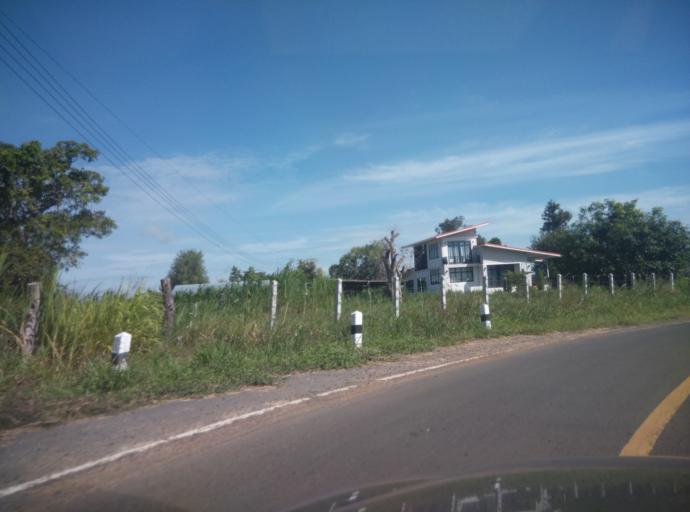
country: TH
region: Sisaket
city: Si Sa Ket
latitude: 15.1195
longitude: 104.2514
